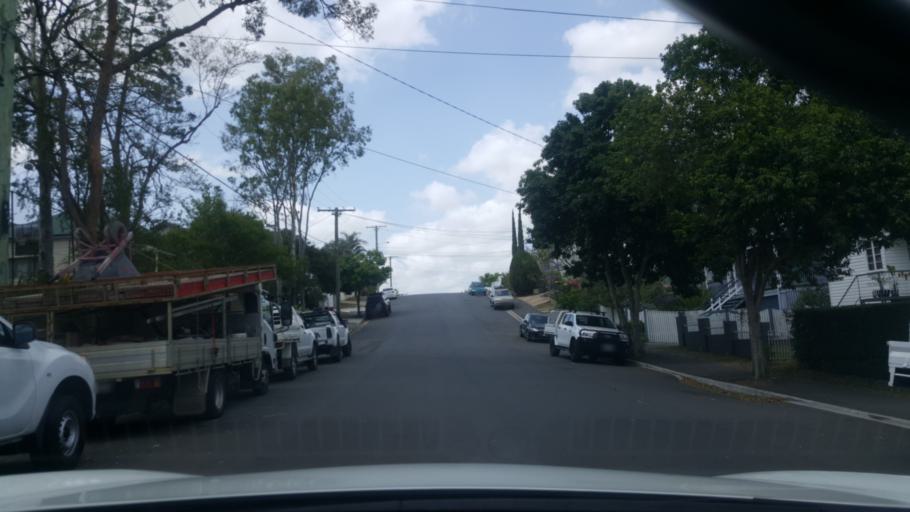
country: AU
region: Queensland
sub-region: Brisbane
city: South Brisbane
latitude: -27.4862
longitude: 153.0227
